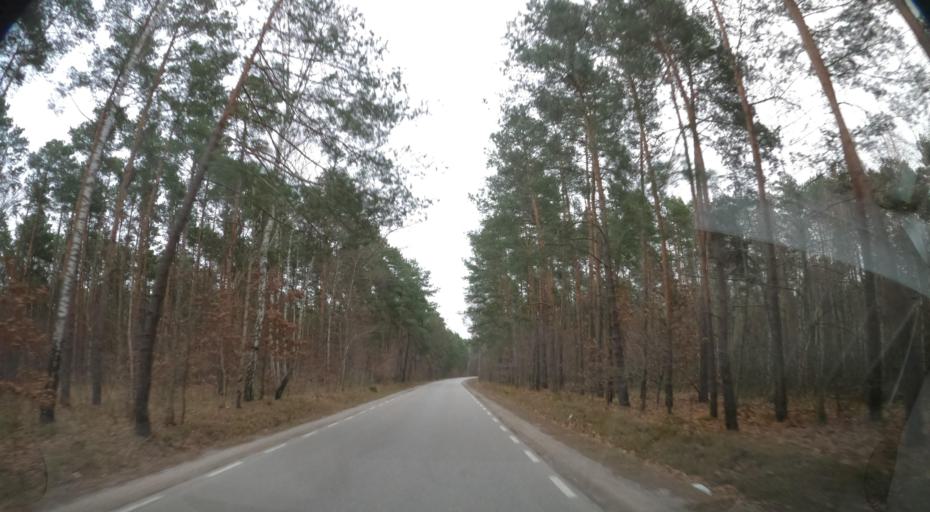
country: PL
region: Masovian Voivodeship
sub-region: Powiat radomski
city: Jedlinsk
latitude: 51.4925
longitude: 21.1531
